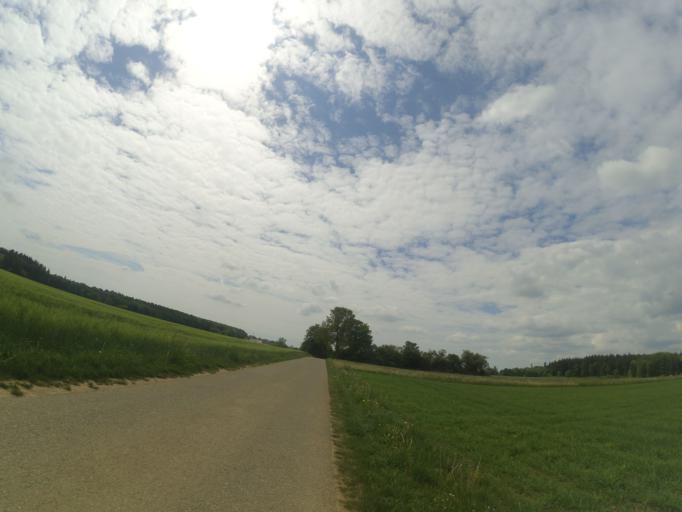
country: DE
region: Baden-Wuerttemberg
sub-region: Tuebingen Region
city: Berghulen
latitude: 48.4414
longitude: 9.7738
